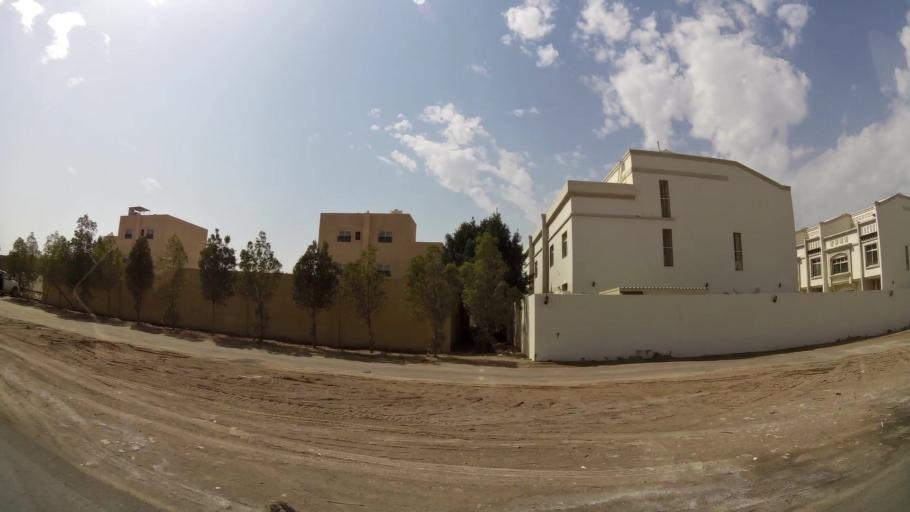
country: AE
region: Abu Dhabi
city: Abu Dhabi
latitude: 24.3462
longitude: 54.5532
